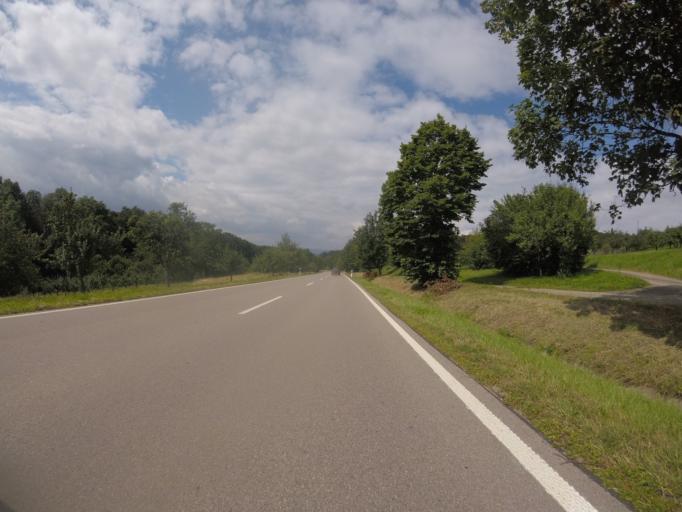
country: DE
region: Baden-Wuerttemberg
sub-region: Regierungsbezirk Stuttgart
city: Winnenden
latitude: 48.8325
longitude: 9.4179
